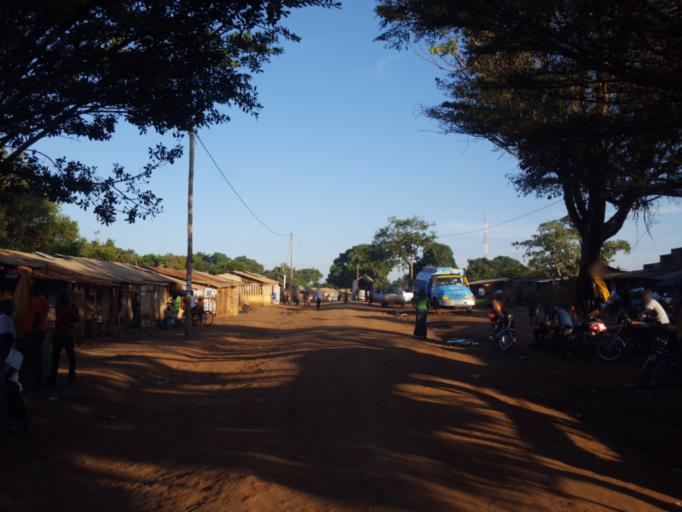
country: UG
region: Western Region
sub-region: Kibale District
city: Kagadi
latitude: 1.1889
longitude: 30.7825
